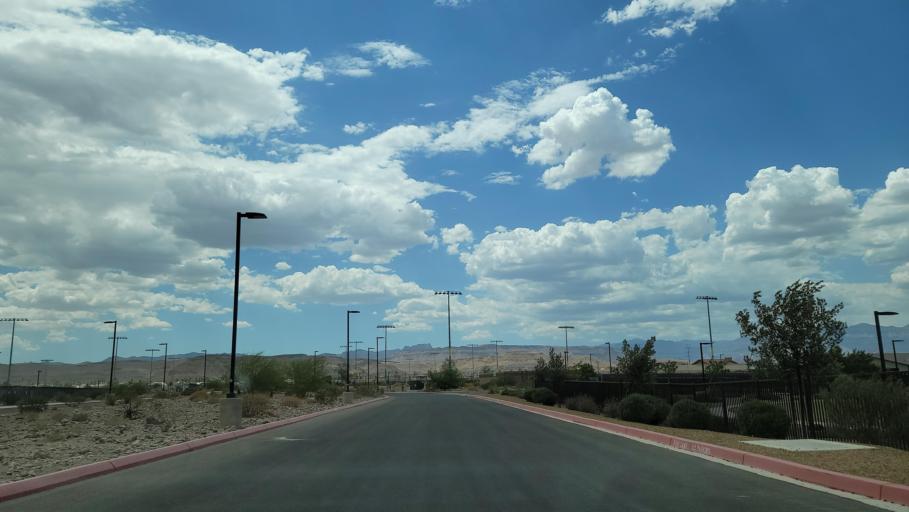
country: US
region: Nevada
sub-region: Clark County
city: Enterprise
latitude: 36.0521
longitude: -115.2713
